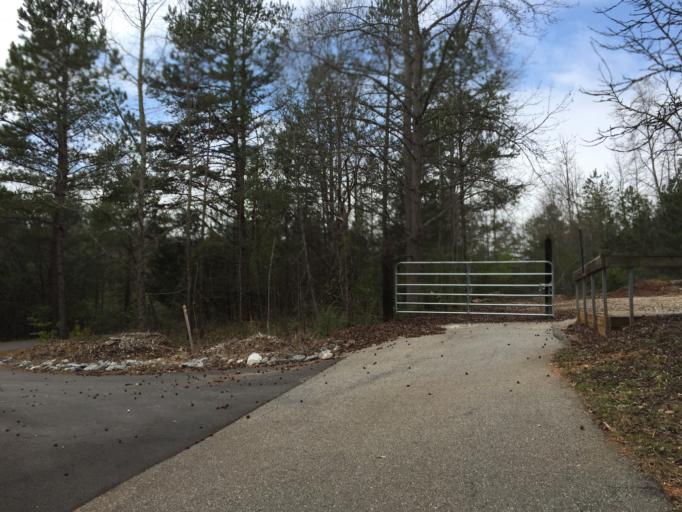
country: US
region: South Carolina
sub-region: Greenville County
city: Mauldin
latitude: 34.7781
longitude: -82.3601
